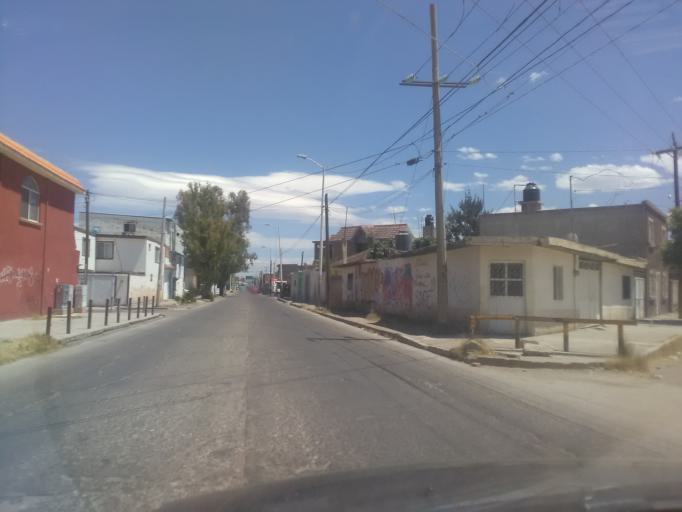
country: MX
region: Durango
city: Victoria de Durango
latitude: 24.0238
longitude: -104.6275
